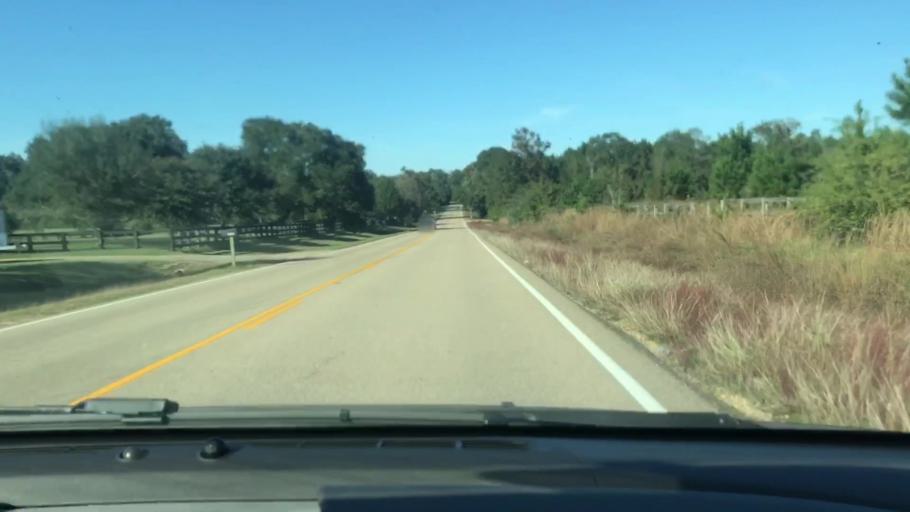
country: US
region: Louisiana
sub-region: Saint Tammany Parish
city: Abita Springs
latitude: 30.5426
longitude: -90.0452
